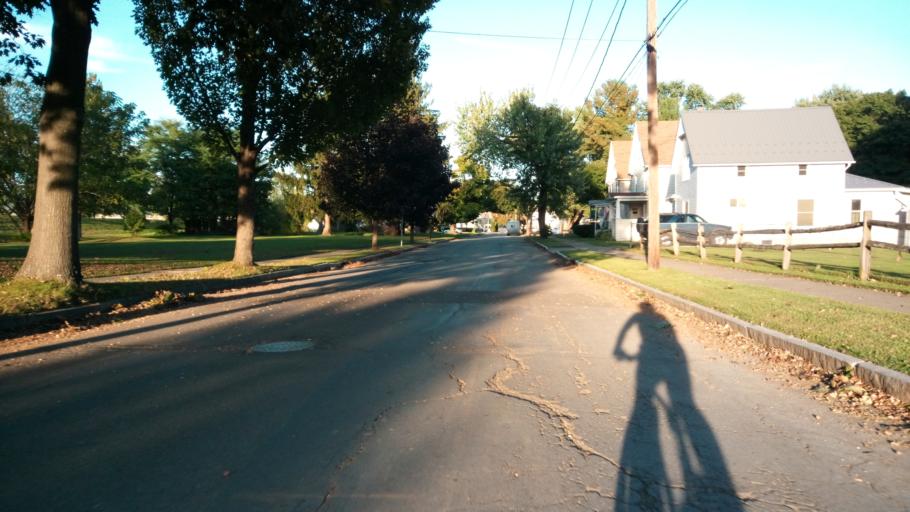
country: US
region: New York
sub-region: Chemung County
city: Elmira
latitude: 42.0806
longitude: -76.8171
